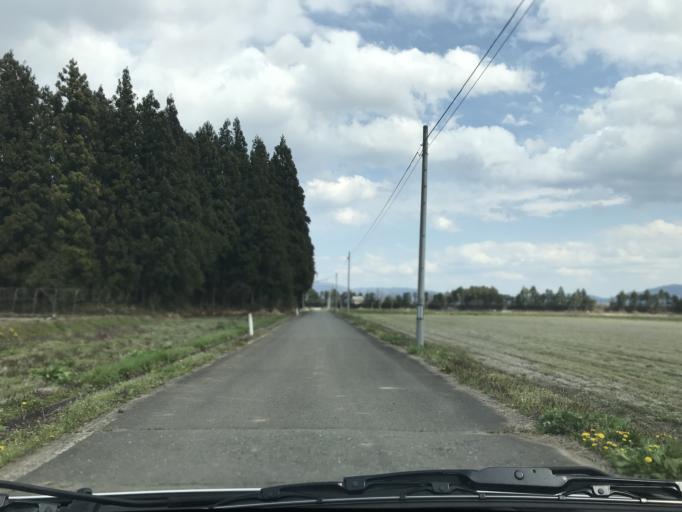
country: JP
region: Iwate
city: Mizusawa
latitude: 39.0804
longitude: 141.0973
